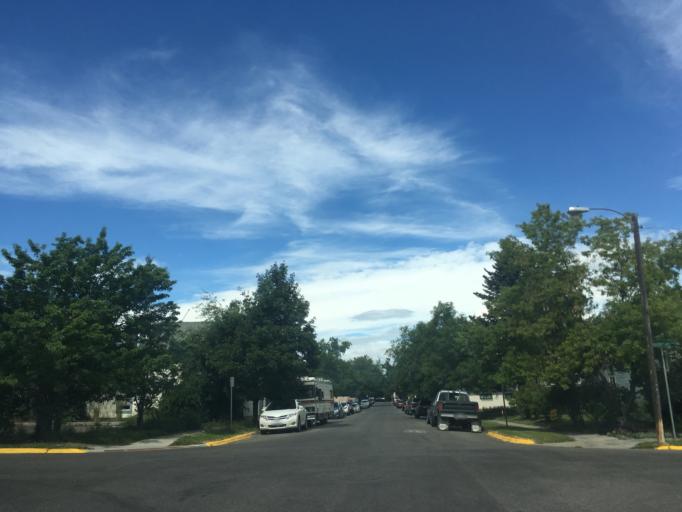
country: US
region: Montana
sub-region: Gallatin County
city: Bozeman
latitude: 45.6815
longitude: -111.0341
